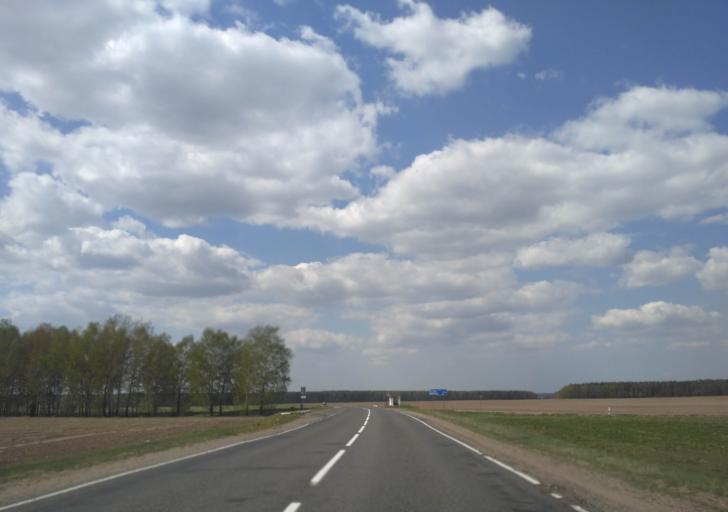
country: BY
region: Minsk
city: Vilyeyka
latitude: 54.5170
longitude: 27.0333
